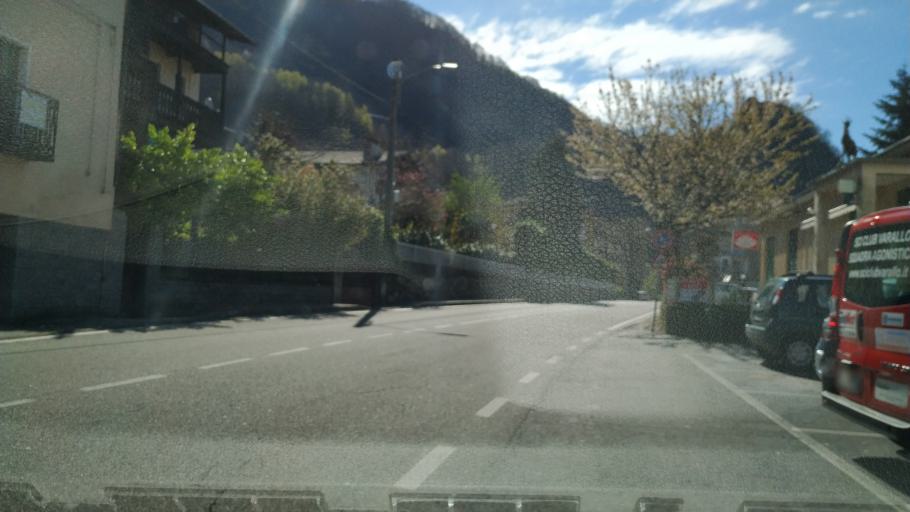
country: IT
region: Piedmont
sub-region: Provincia di Vercelli
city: Civiasco
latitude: 45.7929
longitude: 8.2764
